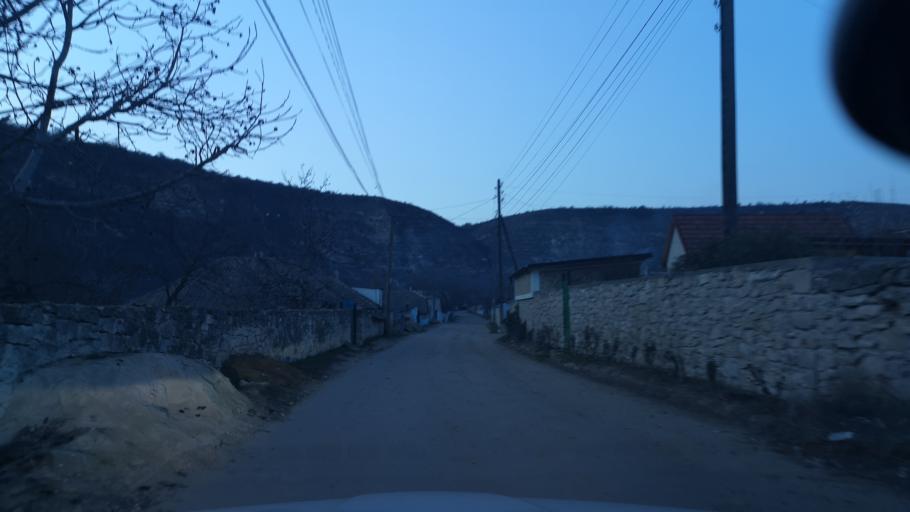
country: MD
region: Telenesti
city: Cocieri
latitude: 47.3032
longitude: 28.9638
